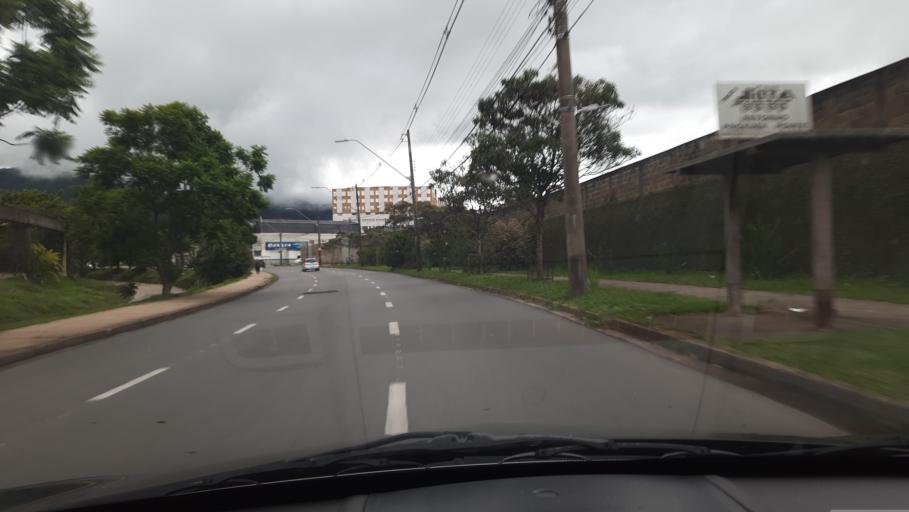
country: BR
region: Minas Gerais
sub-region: Pocos De Caldas
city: Pocos de Caldas
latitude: -21.7817
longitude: -46.5982
